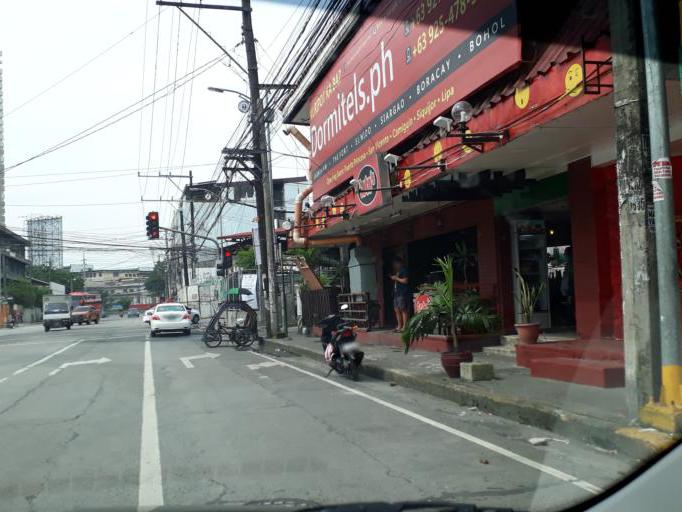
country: PH
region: Metro Manila
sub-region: City of Manila
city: Manila
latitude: 14.6075
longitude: 120.9933
